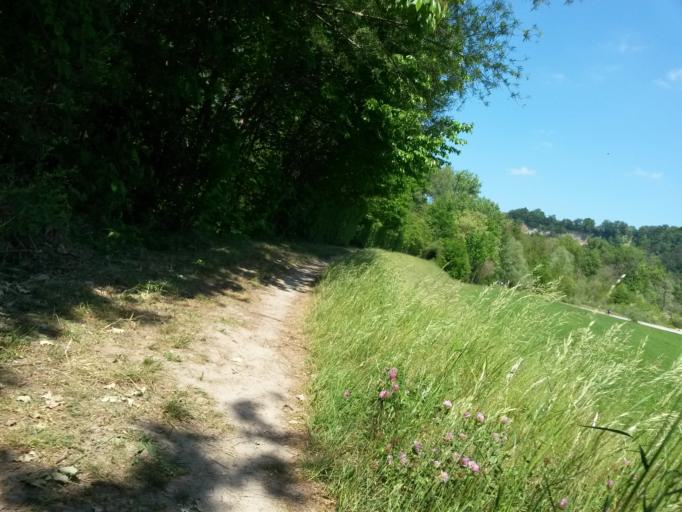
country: CH
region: Bern
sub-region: Bern-Mittelland District
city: Muhleberg
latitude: 46.9770
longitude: 7.2527
